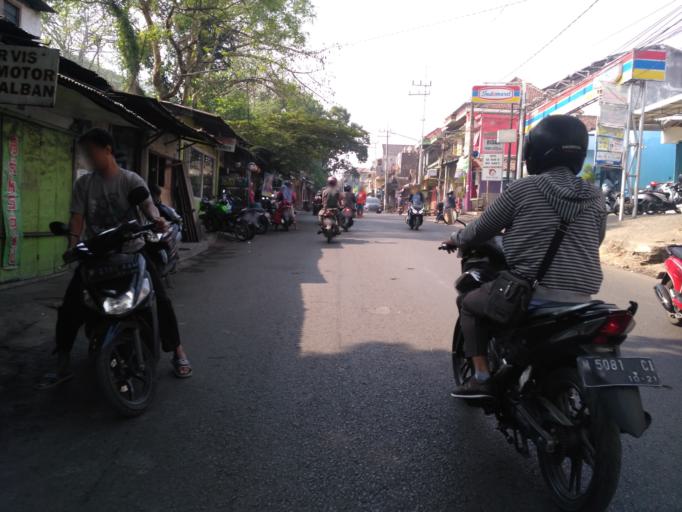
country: ID
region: East Java
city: Malang
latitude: -7.9911
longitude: 112.6417
